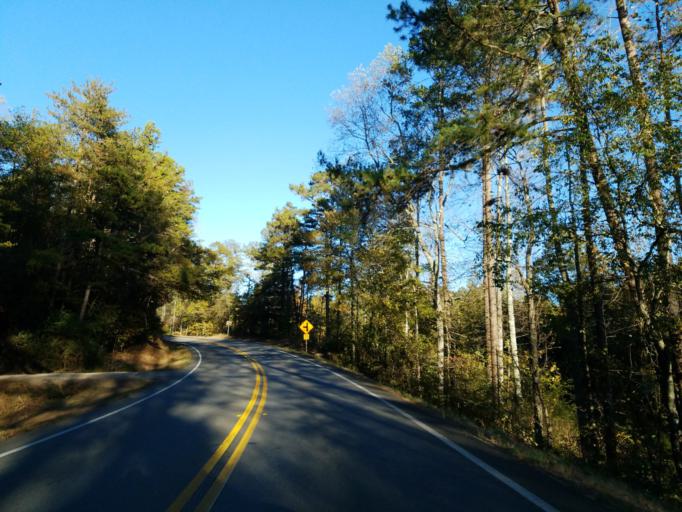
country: US
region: Georgia
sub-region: Dawson County
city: Dawsonville
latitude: 34.4296
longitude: -84.1790
